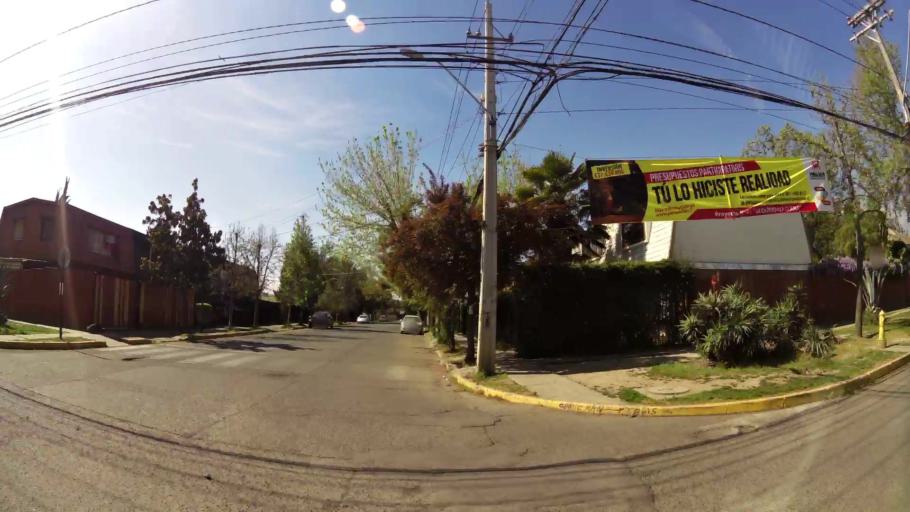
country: CL
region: Santiago Metropolitan
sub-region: Provincia de Santiago
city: Villa Presidente Frei, Nunoa, Santiago, Chile
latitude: -33.4945
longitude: -70.5790
